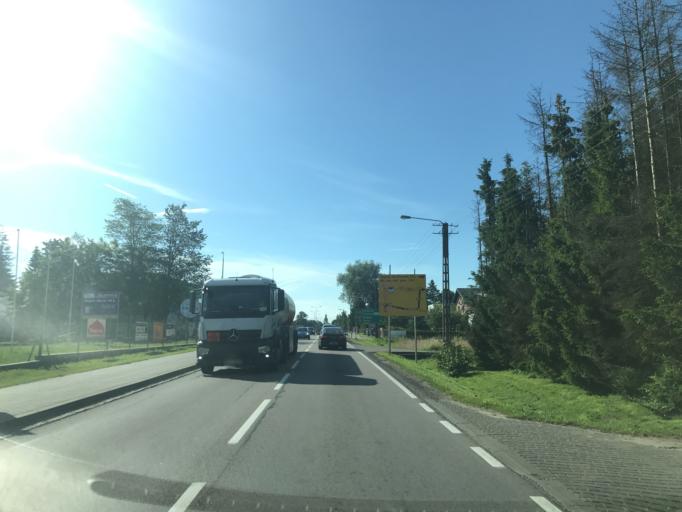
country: PL
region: Pomeranian Voivodeship
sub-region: Powiat czluchowski
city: Czluchow
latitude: 53.6726
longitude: 17.3483
